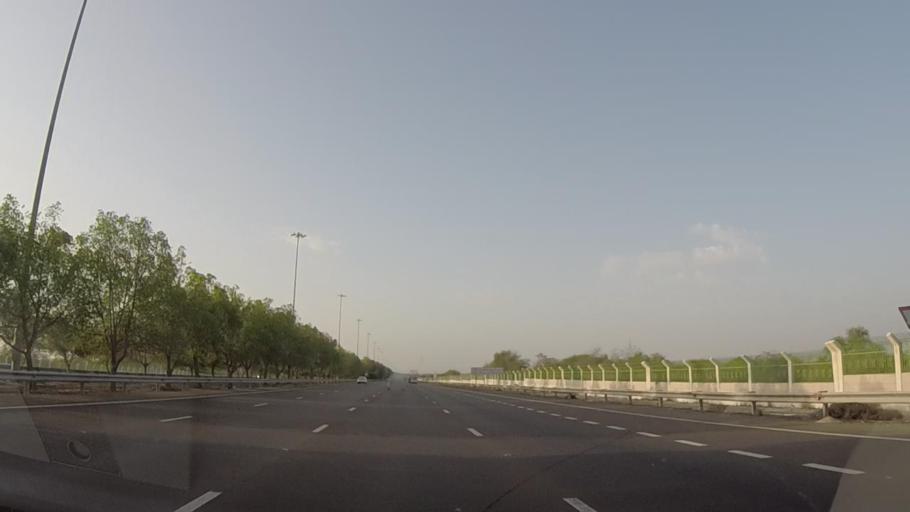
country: AE
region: Dubai
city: Dubai
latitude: 24.7919
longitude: 54.8598
